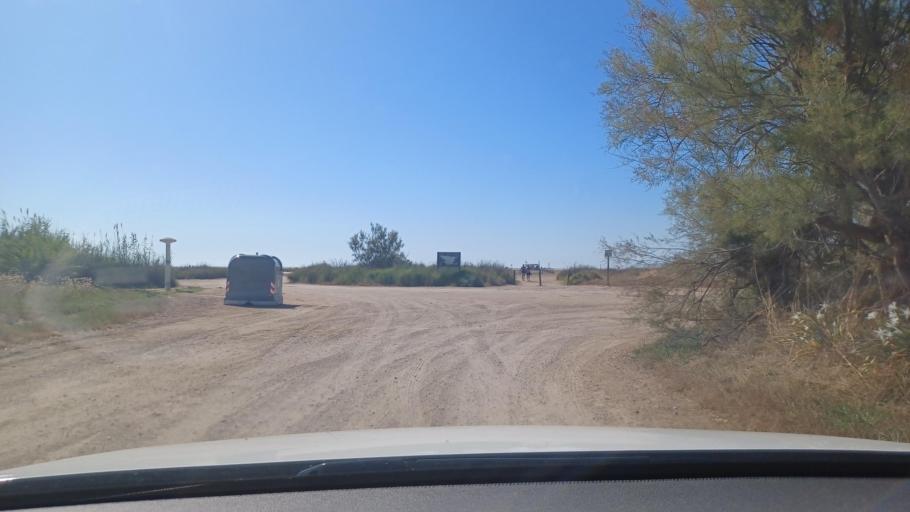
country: ES
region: Catalonia
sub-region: Provincia de Tarragona
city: Deltebre
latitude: 40.6559
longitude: 0.7828
